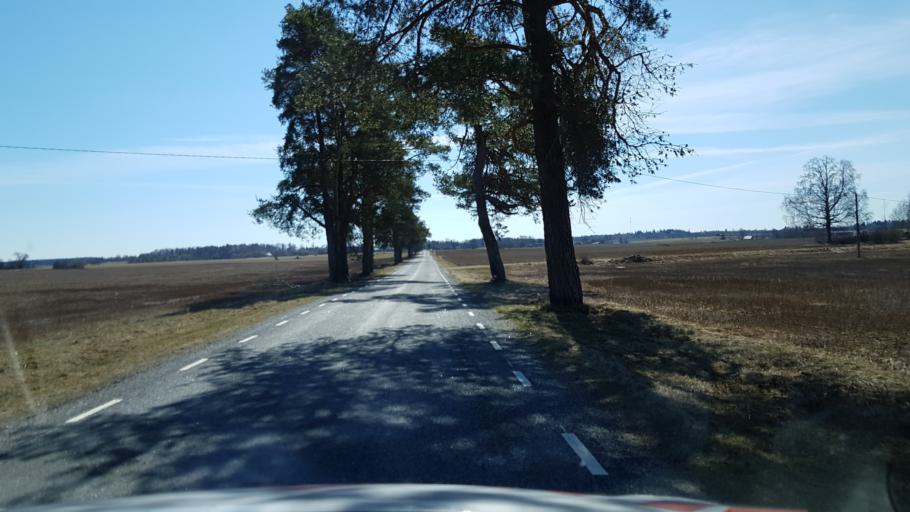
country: EE
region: Laeaene-Virumaa
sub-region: Vinni vald
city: Vinni
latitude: 59.1122
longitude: 26.5242
